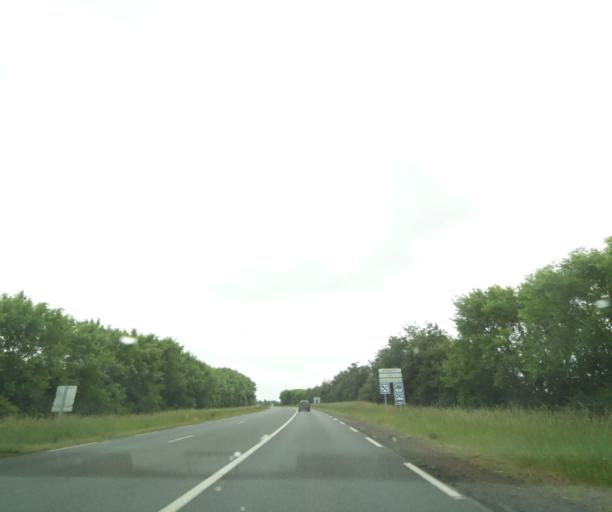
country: FR
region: Poitou-Charentes
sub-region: Departement des Deux-Sevres
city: Airvault
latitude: 46.8180
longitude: -0.2060
